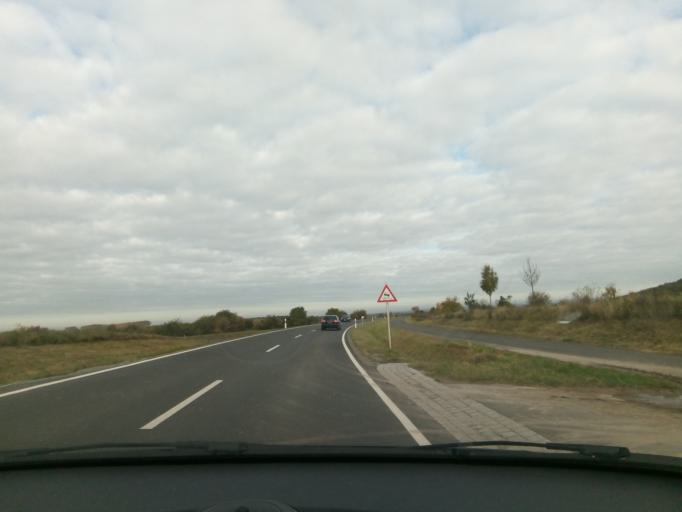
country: DE
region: Bavaria
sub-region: Regierungsbezirk Unterfranken
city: Dingolshausen
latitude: 49.8814
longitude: 10.3792
